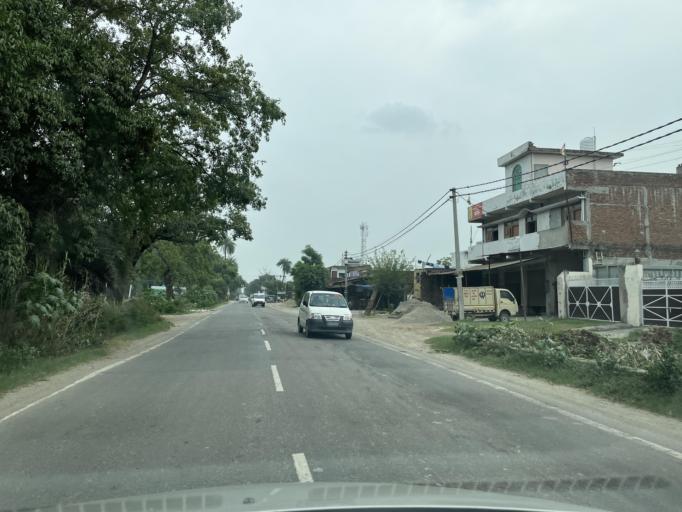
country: IN
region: Uttar Pradesh
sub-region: Rampur
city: Bilaspur
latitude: 29.0325
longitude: 79.2604
